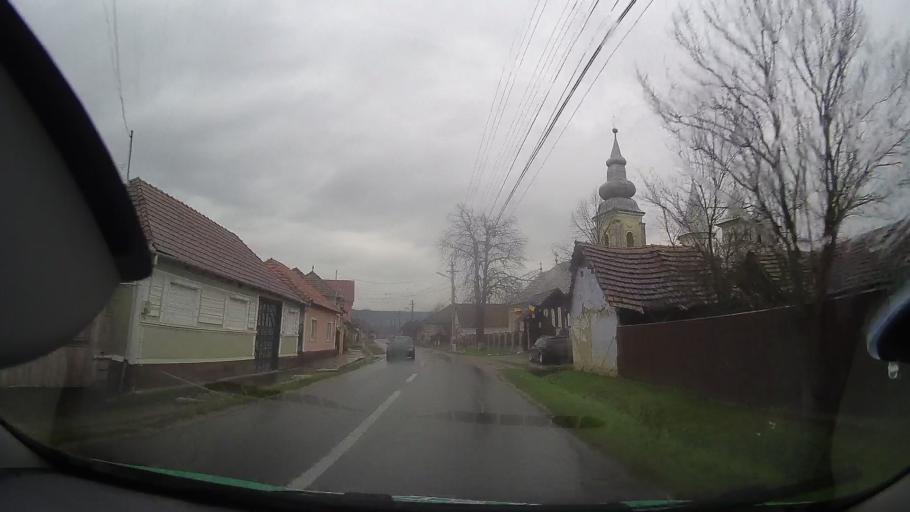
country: RO
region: Bihor
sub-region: Comuna Rabagani
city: Rabagani
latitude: 46.7479
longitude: 22.2315
